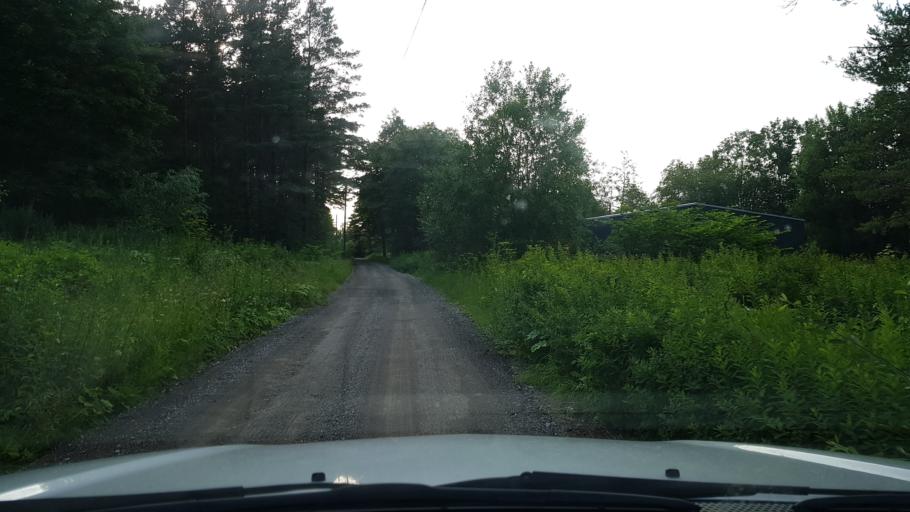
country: EE
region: Ida-Virumaa
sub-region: Narva-Joesuu linn
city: Narva-Joesuu
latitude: 59.4573
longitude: 28.0668
